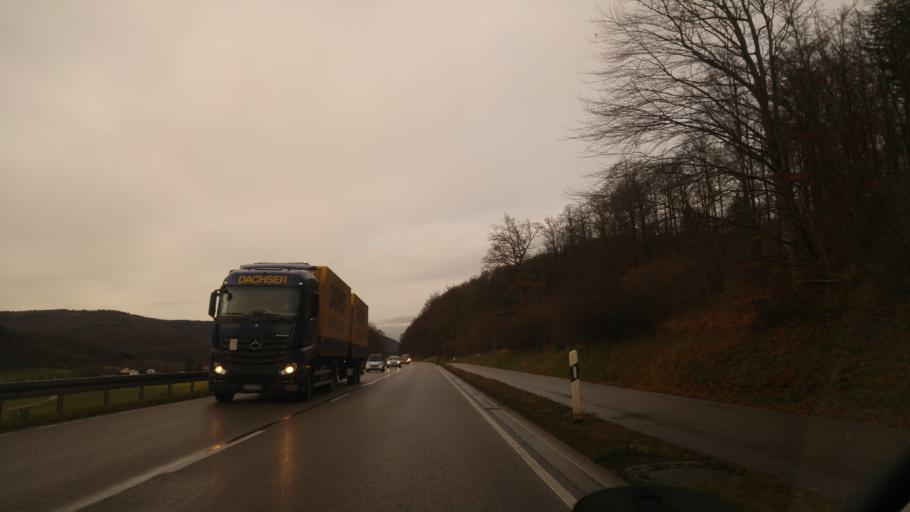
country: DE
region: Baden-Wuerttemberg
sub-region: Regierungsbezirk Stuttgart
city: Konigsbronn
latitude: 48.7520
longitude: 10.1033
